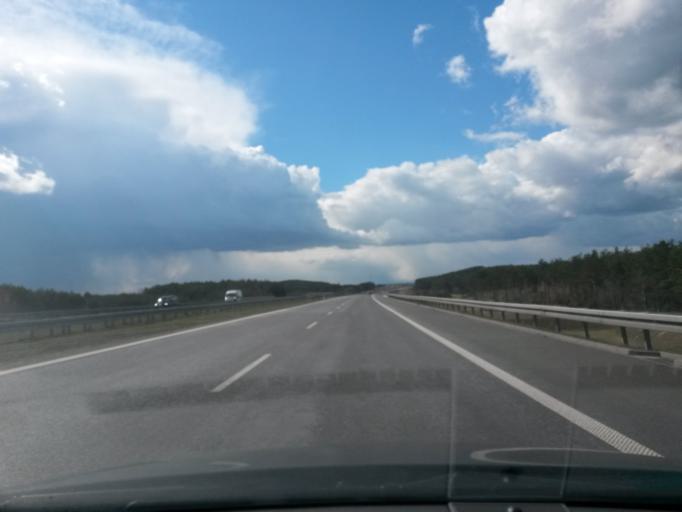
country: PL
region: Greater Poland Voivodeship
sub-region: Powiat kolski
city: Koscielec
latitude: 52.1416
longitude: 18.5432
